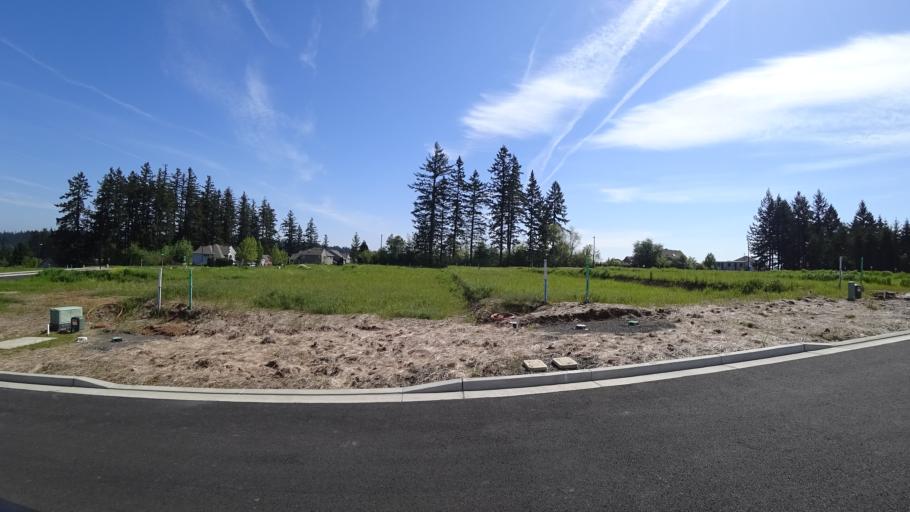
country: US
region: Oregon
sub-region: Washington County
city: King City
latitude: 45.4357
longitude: -122.8417
